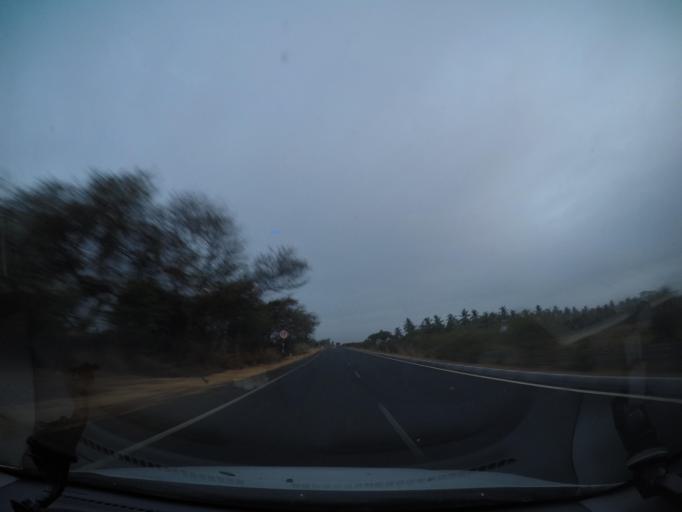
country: IN
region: Andhra Pradesh
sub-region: West Godavari
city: Tadepallegudem
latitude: 16.8100
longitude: 81.3512
